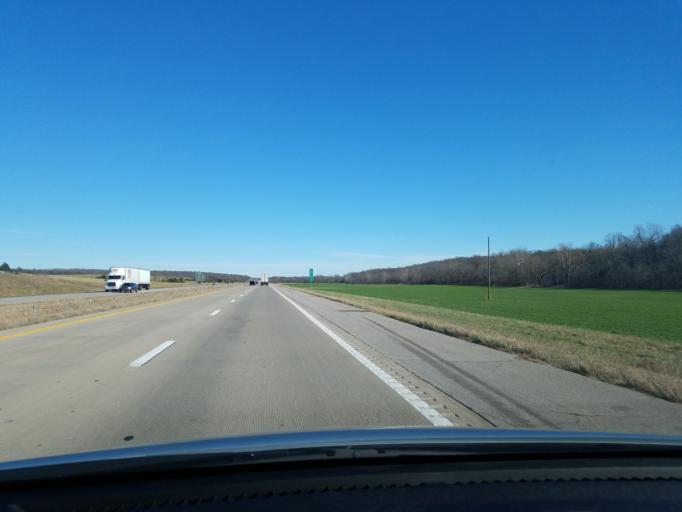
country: US
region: Missouri
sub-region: Laclede County
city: Lebanon
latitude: 37.7519
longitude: -92.5710
